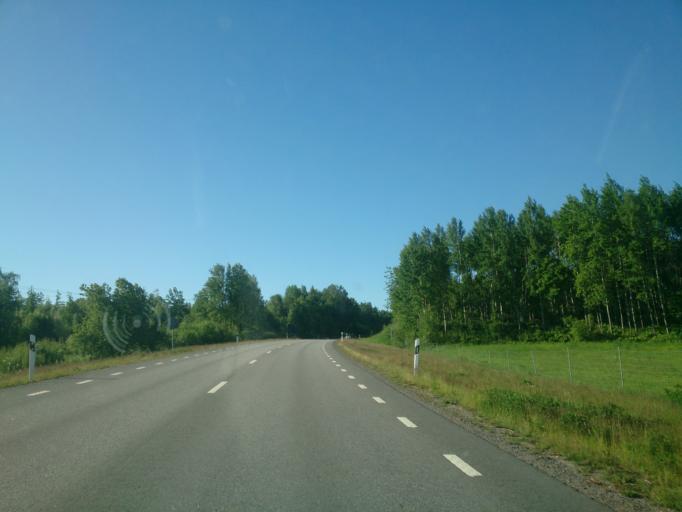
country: SE
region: OEstergoetland
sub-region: Atvidabergs Kommun
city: Atvidaberg
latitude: 58.1905
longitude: 16.0232
